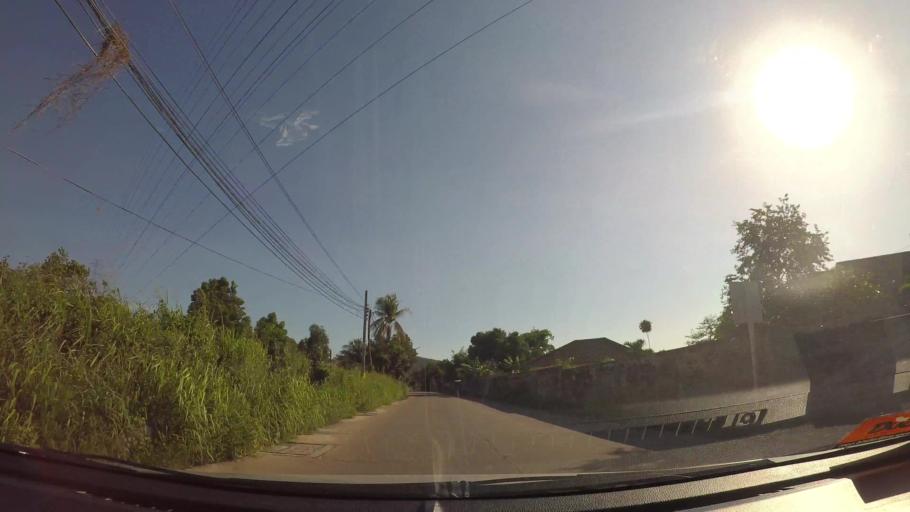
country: TH
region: Chon Buri
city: Si Racha
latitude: 13.1473
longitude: 100.9417
